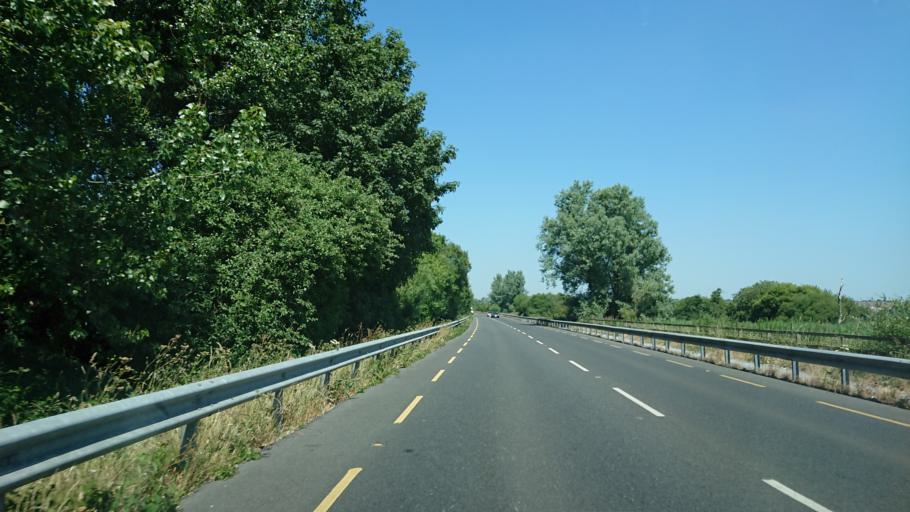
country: IE
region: Munster
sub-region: Waterford
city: Waterford
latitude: 52.2288
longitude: -7.1233
